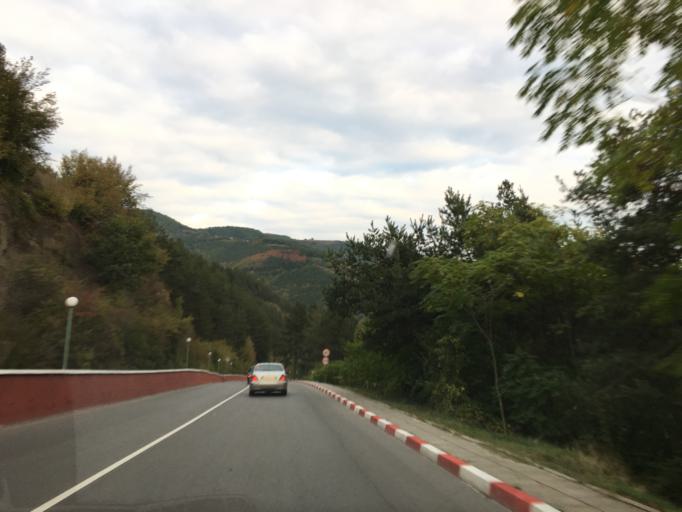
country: BG
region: Sofiya
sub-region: Obshtina Svoge
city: Svoge
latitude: 42.9534
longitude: 23.3680
